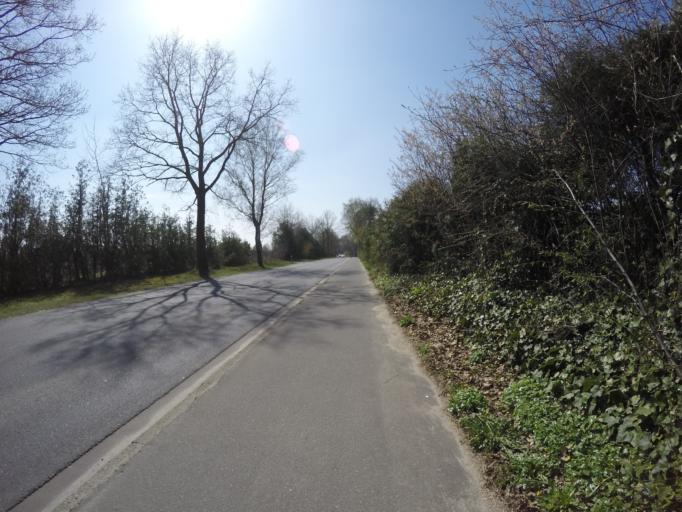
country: DE
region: Schleswig-Holstein
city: Quickborn
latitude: 53.7283
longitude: 9.9308
